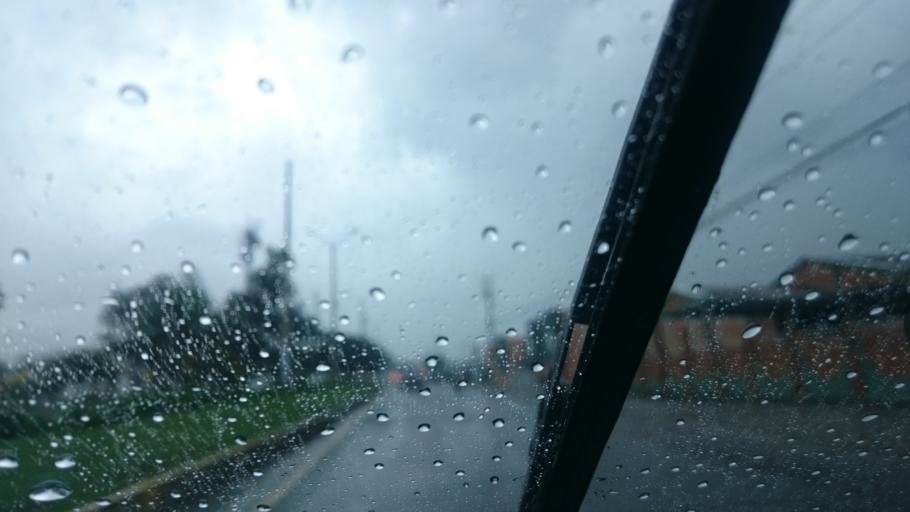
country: CO
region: Cauca
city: Popayan
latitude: 2.4898
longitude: -76.5600
